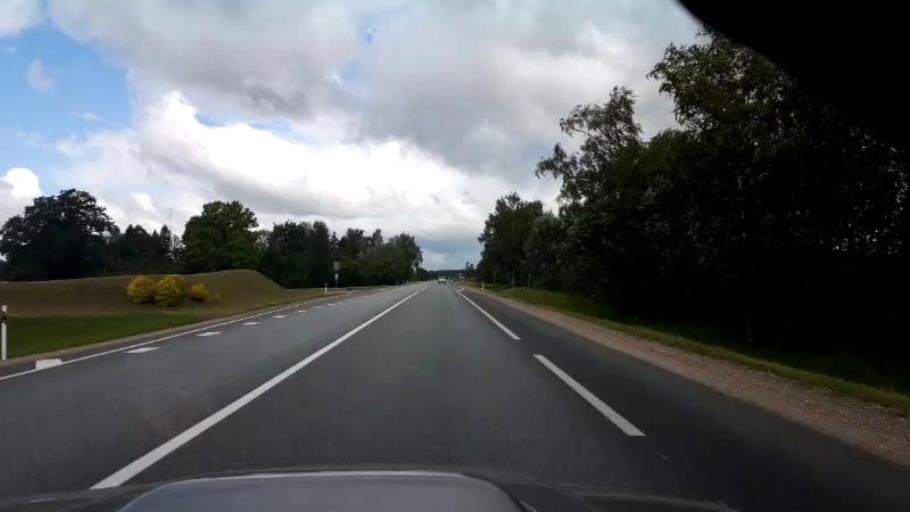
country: LV
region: Bauskas Rajons
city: Bauska
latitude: 56.4399
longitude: 24.1714
